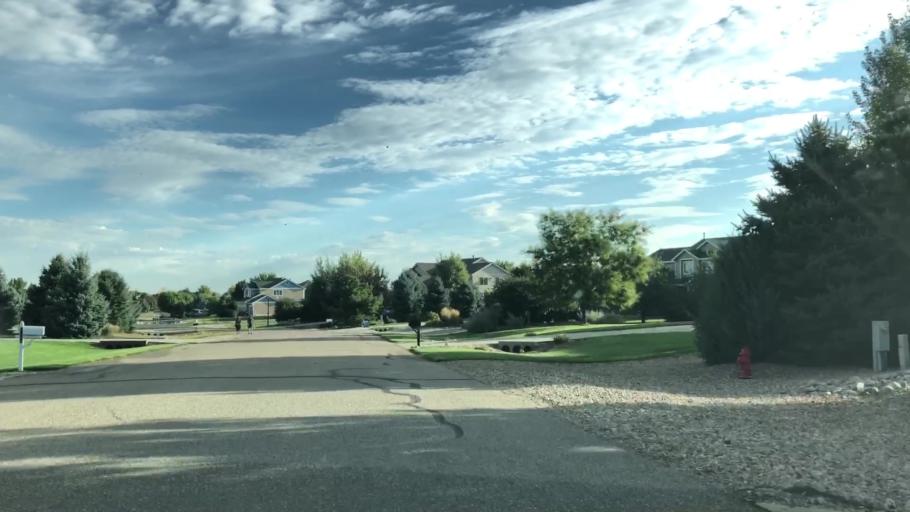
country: US
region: Colorado
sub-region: Weld County
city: Windsor
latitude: 40.4407
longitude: -104.9617
